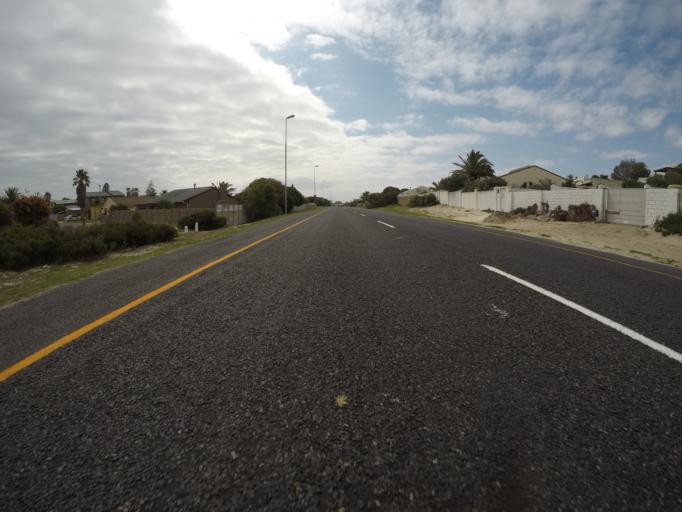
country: ZA
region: Western Cape
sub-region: City of Cape Town
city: Sunset Beach
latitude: -33.7208
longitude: 18.4467
